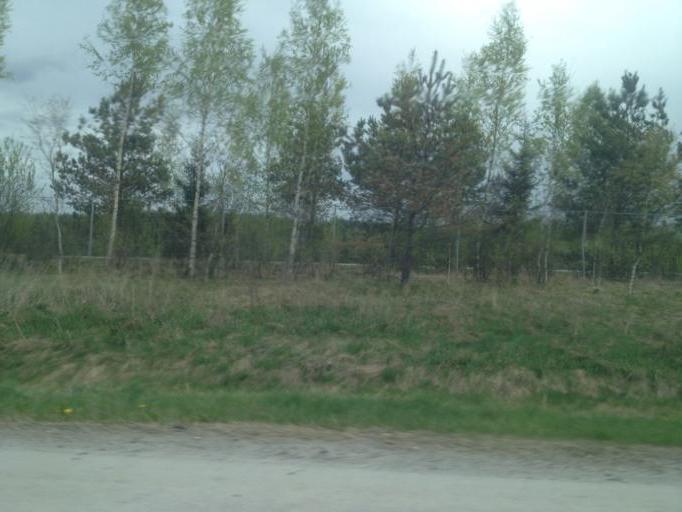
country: FI
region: Uusimaa
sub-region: Helsinki
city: Hyvinge
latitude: 60.5991
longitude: 24.7988
